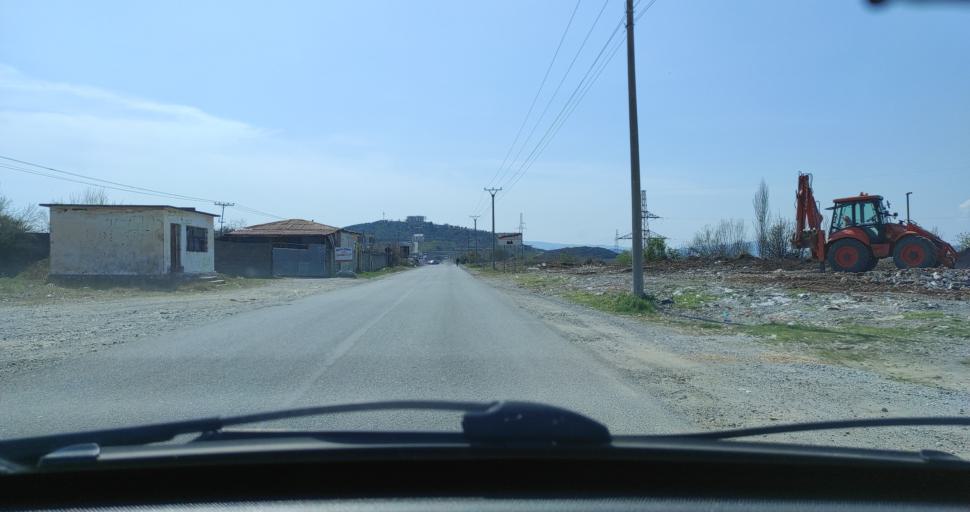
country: AL
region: Shkoder
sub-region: Rrethi i Shkodres
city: Vau i Dejes
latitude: 42.0068
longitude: 19.6359
